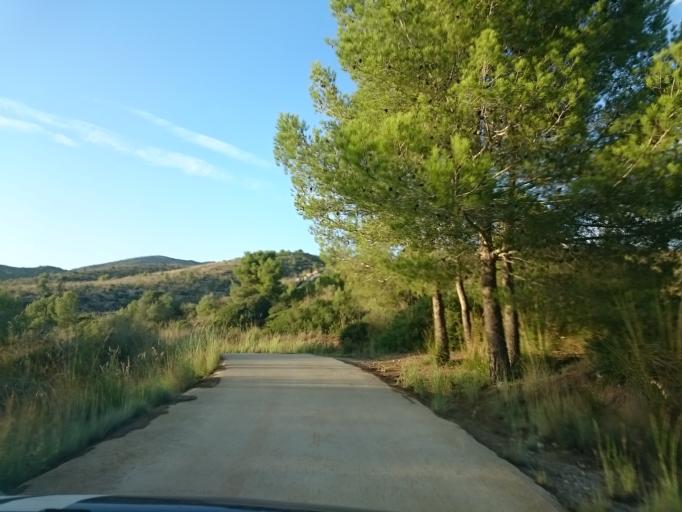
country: ES
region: Catalonia
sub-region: Provincia de Barcelona
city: Olivella
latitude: 41.2987
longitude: 1.8548
